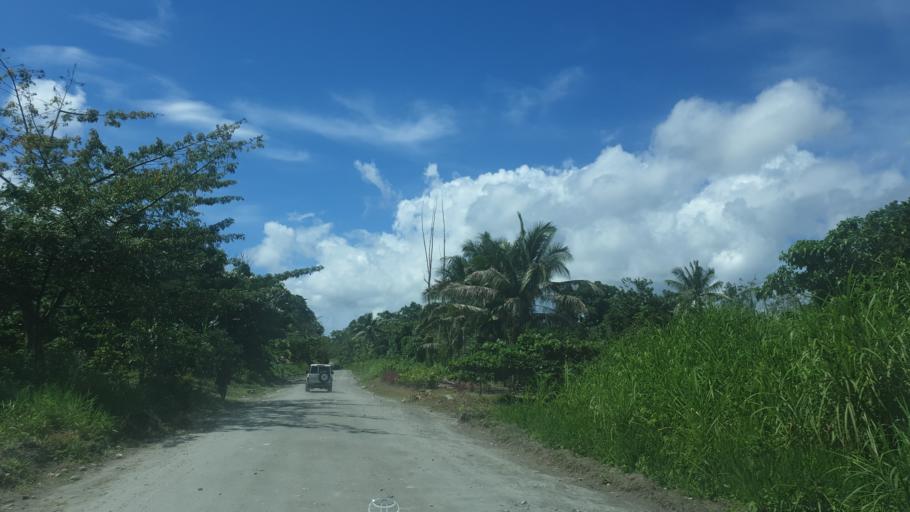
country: PG
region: Bougainville
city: Panguna
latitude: -6.6601
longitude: 155.4469
